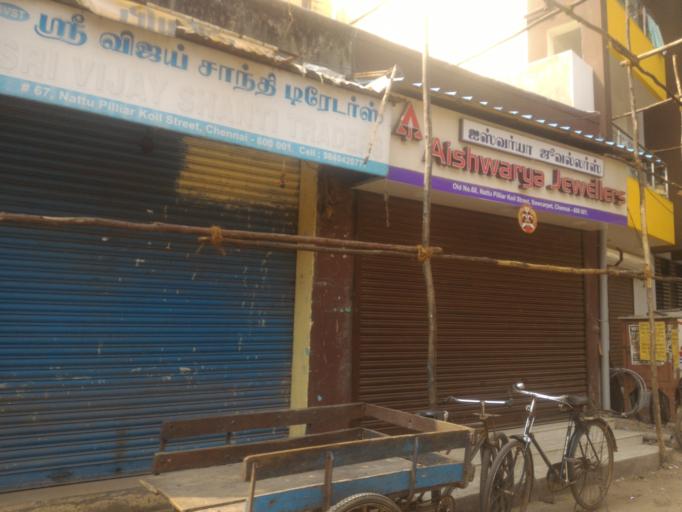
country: IN
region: Tamil Nadu
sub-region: Chennai
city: George Town
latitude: 13.0961
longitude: 80.2807
